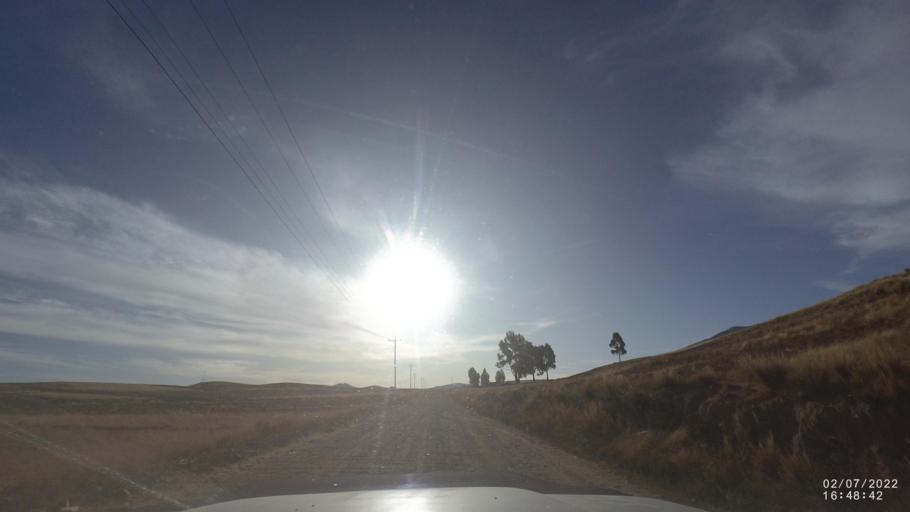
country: BO
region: Cochabamba
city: Irpa Irpa
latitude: -17.9772
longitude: -66.5212
